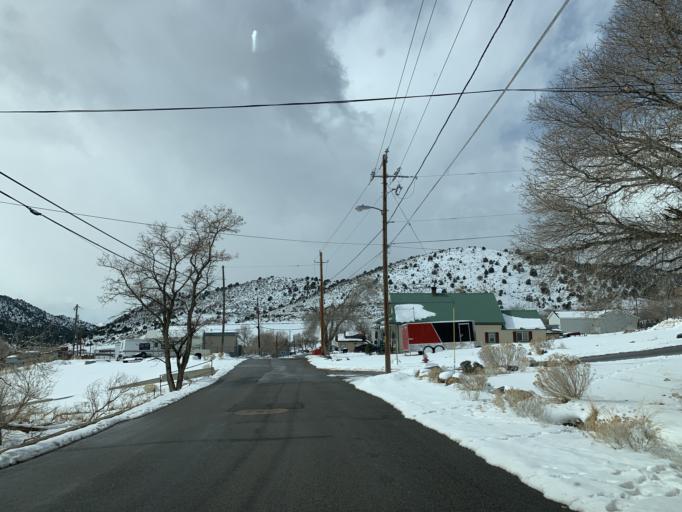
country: US
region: Utah
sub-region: Utah County
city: Genola
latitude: 39.9556
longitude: -112.1194
